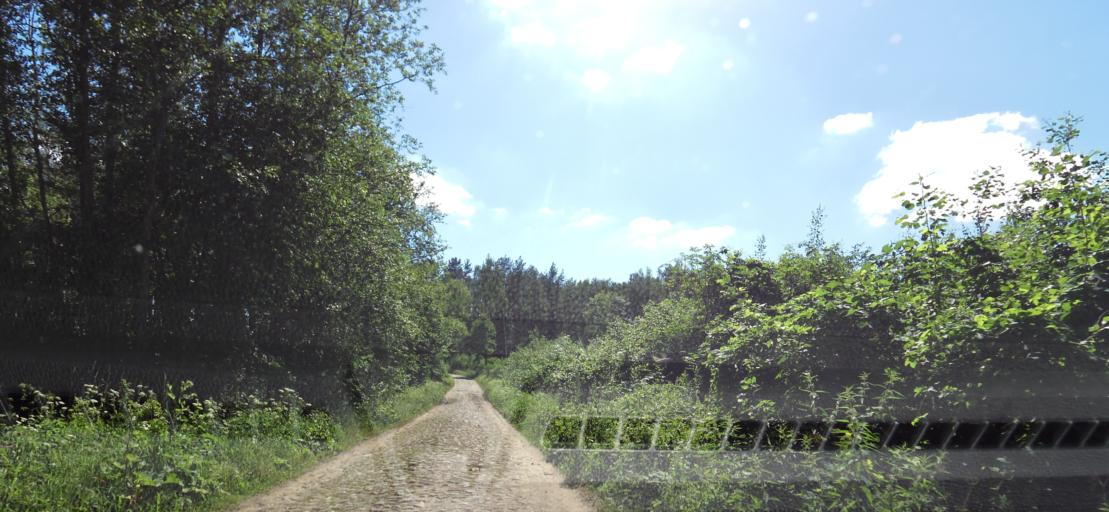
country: LT
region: Vilnius County
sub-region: Vilnius
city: Fabijoniskes
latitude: 54.8401
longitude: 25.3278
